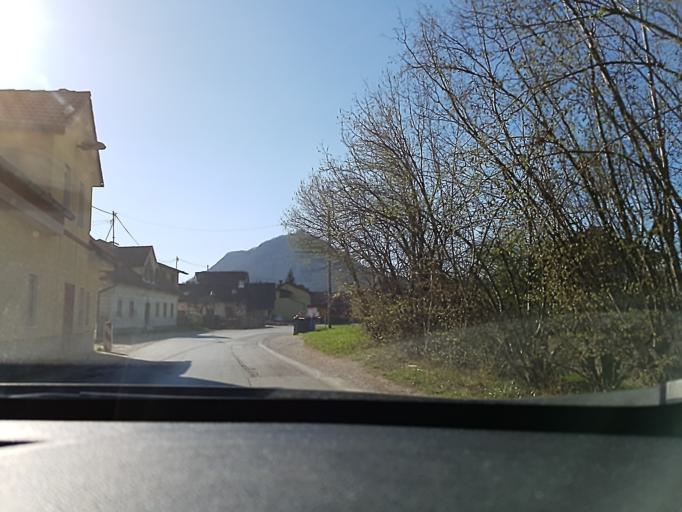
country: SI
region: Medvode
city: Zgornje Pirnice
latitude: 46.1271
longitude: 14.4918
